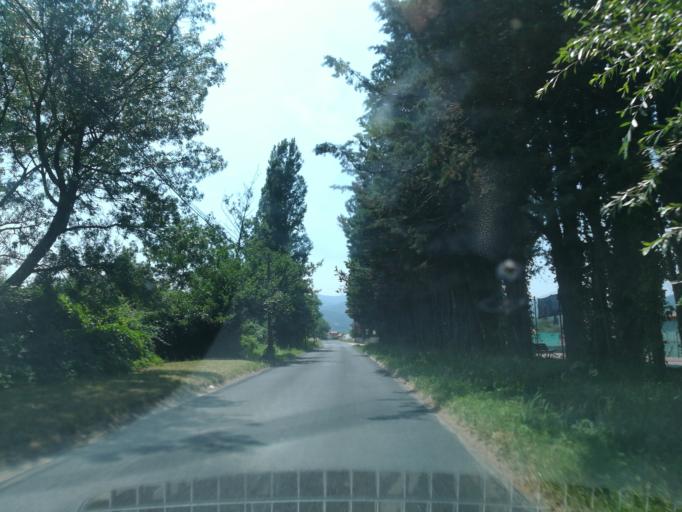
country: FR
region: Languedoc-Roussillon
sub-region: Departement des Pyrenees-Orientales
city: Maureillas-las-Illas
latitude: 42.4948
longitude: 2.8014
